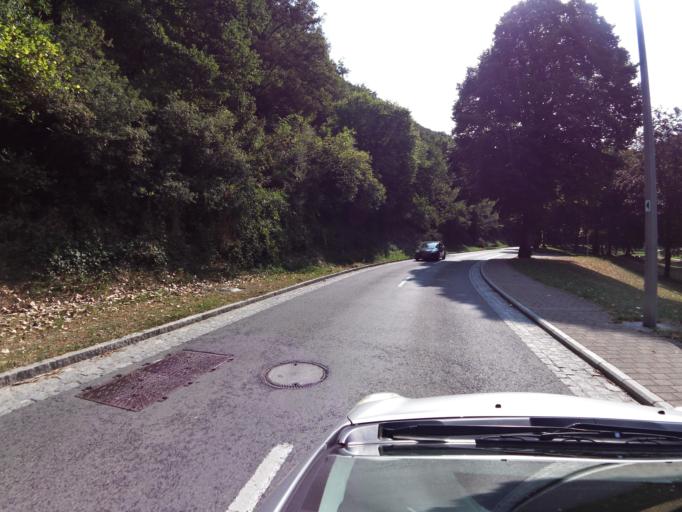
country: LU
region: Diekirch
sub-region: Canton de Wiltz
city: Esch-sur-Sure
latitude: 49.9096
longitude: 5.9374
